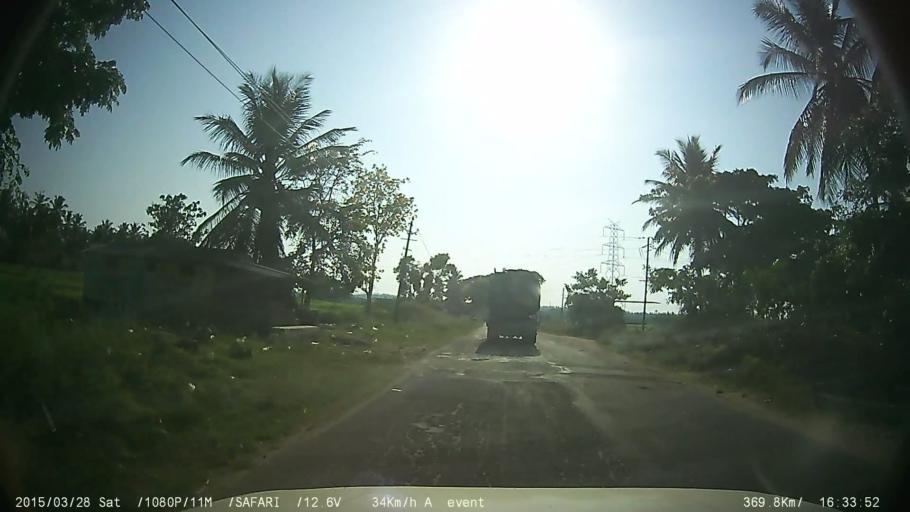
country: IN
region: Karnataka
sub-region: Mandya
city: Shrirangapattana
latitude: 12.3923
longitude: 76.6228
